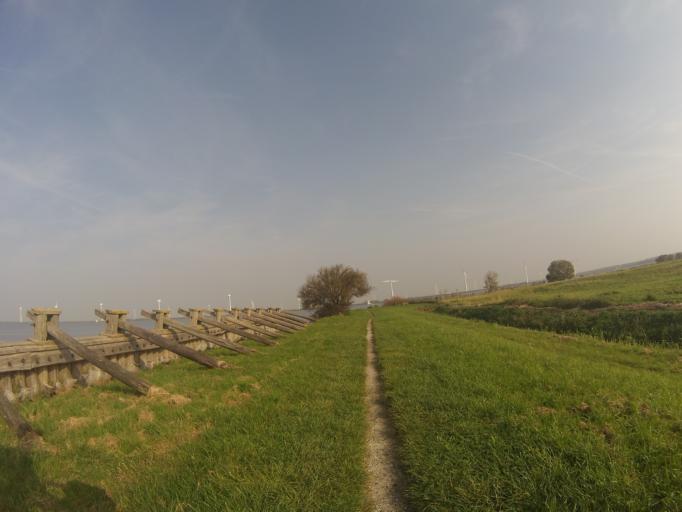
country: NL
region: Utrecht
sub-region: Gemeente Bunschoten
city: Spakenburg
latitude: 52.2694
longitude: 5.3562
